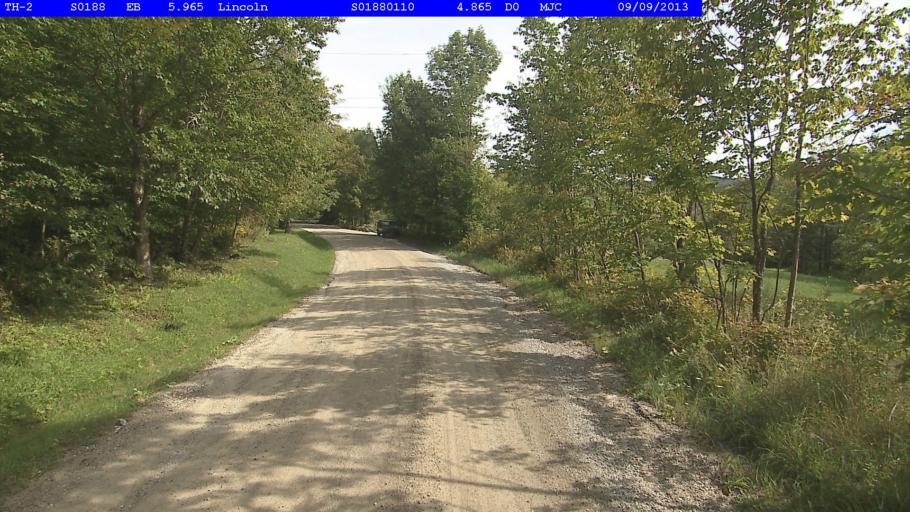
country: US
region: Vermont
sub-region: Addison County
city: Bristol
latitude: 44.0919
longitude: -72.9568
